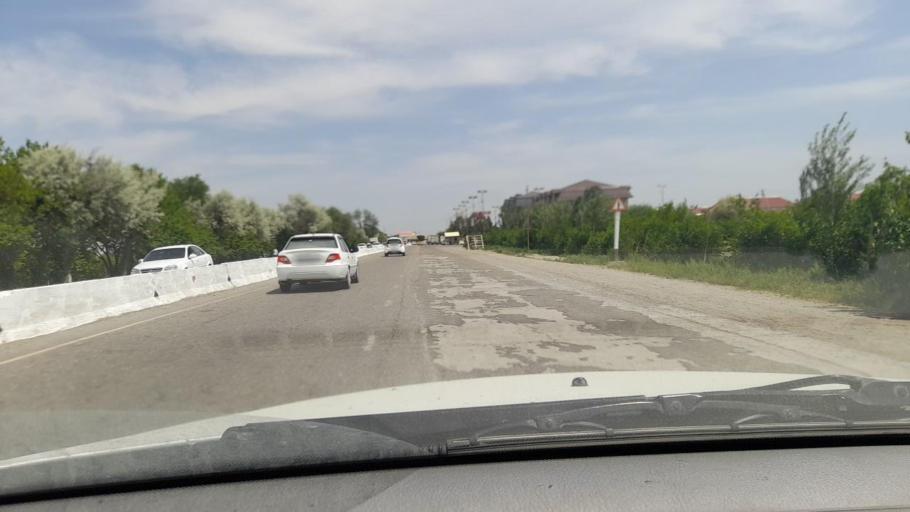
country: UZ
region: Bukhara
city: Wobkent
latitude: 40.0673
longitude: 64.5564
